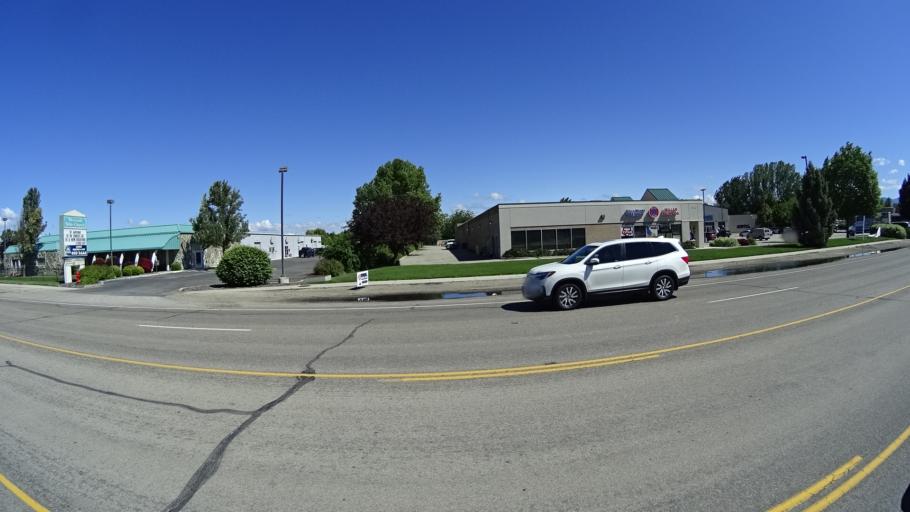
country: US
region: Idaho
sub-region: Ada County
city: Meridian
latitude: 43.6194
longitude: -116.3687
